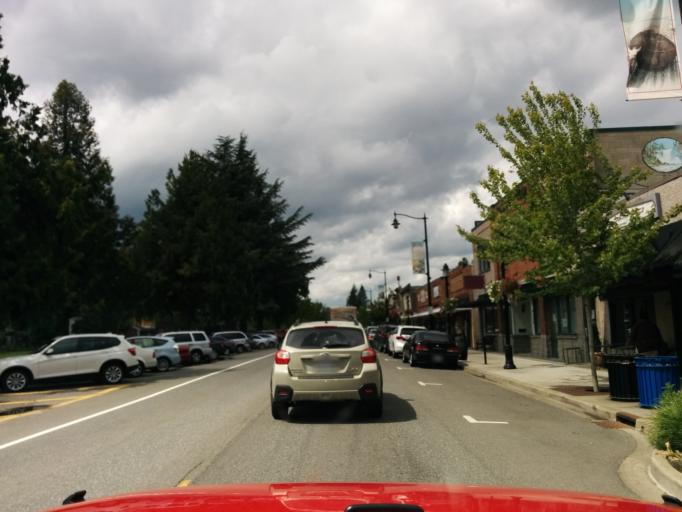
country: US
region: Washington
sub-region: King County
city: Snoqualmie
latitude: 47.5273
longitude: -121.8243
